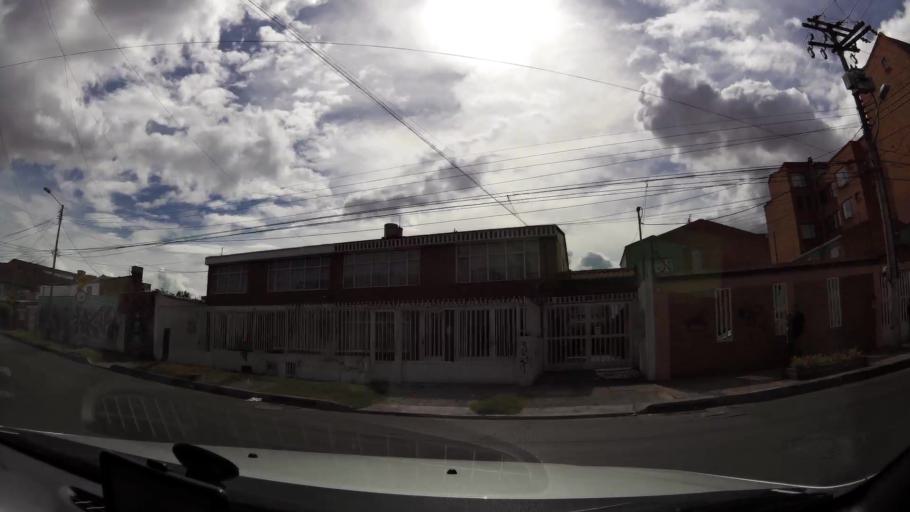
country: CO
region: Bogota D.C.
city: Bogota
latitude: 4.6276
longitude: -74.1356
